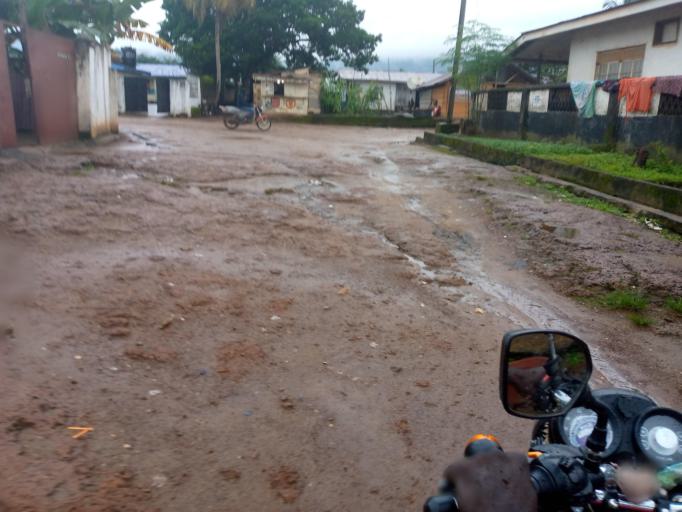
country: SL
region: Eastern Province
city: Kenema
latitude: 7.8843
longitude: -11.1839
